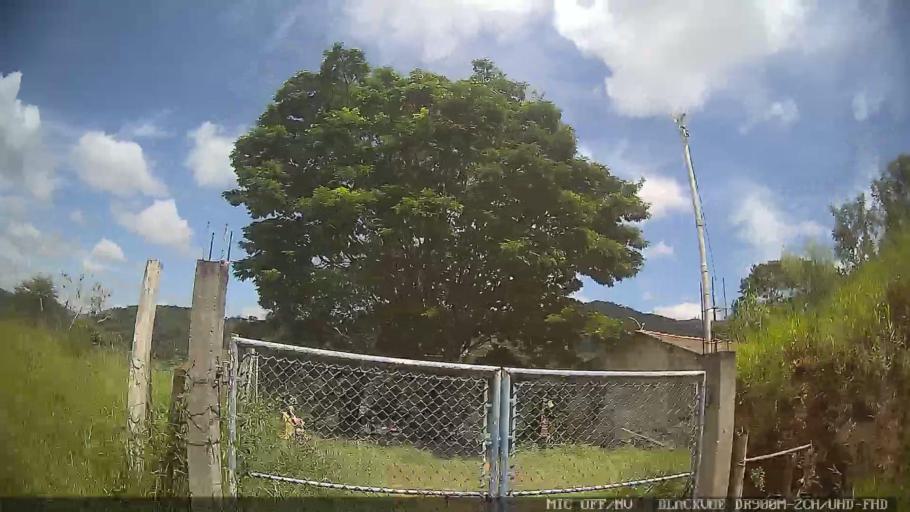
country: BR
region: Sao Paulo
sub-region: Braganca Paulista
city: Braganca Paulista
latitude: -23.0257
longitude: -46.5445
